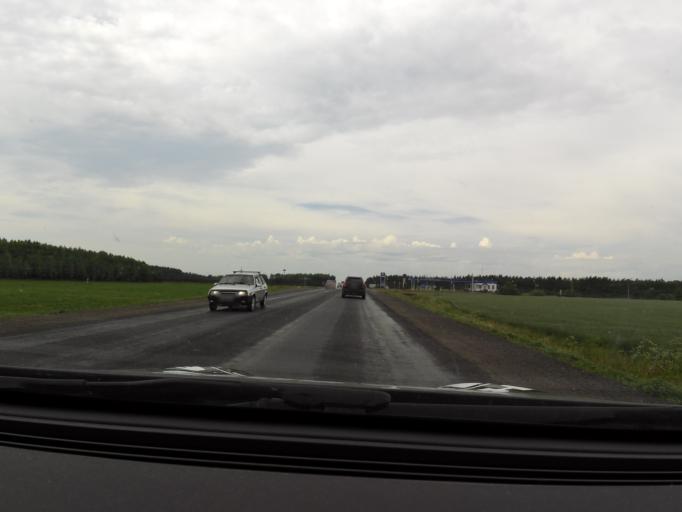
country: RU
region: Bashkortostan
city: Iglino
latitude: 54.7467
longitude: 56.3187
